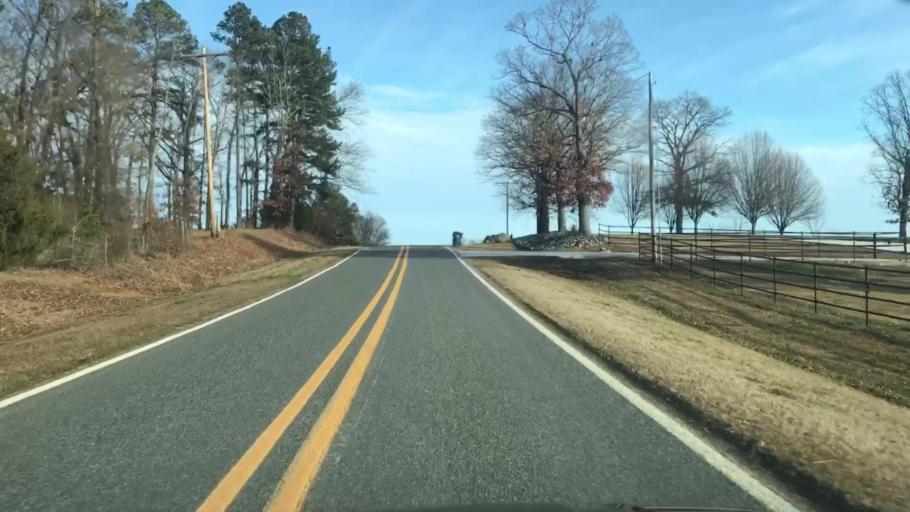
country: US
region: Arkansas
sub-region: Garland County
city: Rockwell
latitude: 34.5022
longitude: -93.2763
